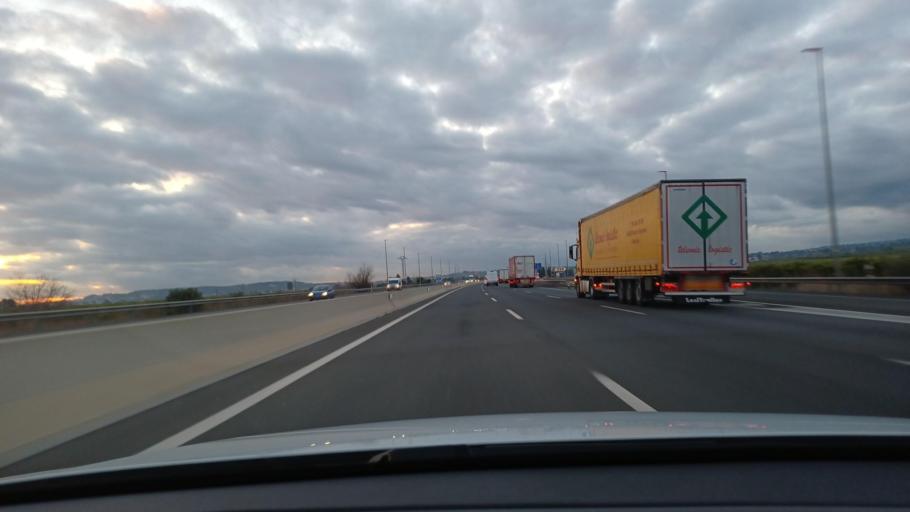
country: ES
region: Valencia
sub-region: Provincia de Valencia
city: Torrent
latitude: 39.4487
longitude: -0.5463
